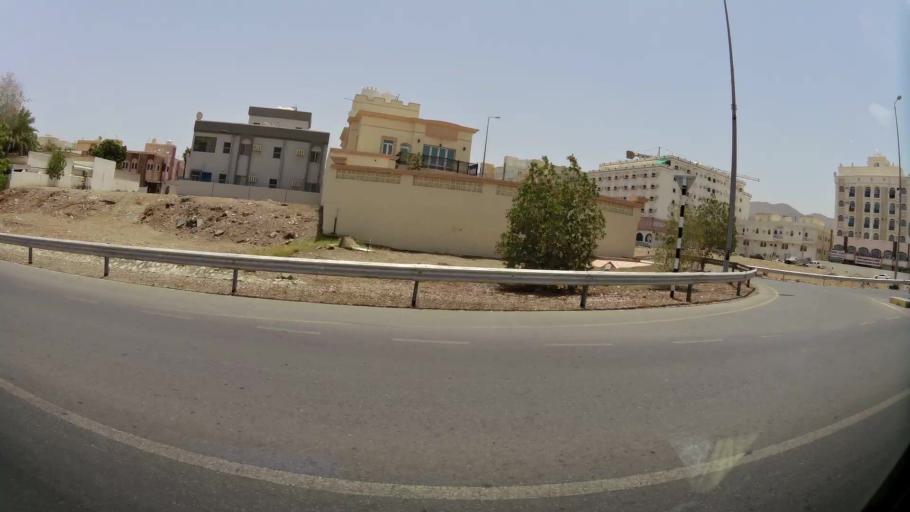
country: OM
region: Muhafazat Masqat
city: Bawshar
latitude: 23.5835
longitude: 58.4217
